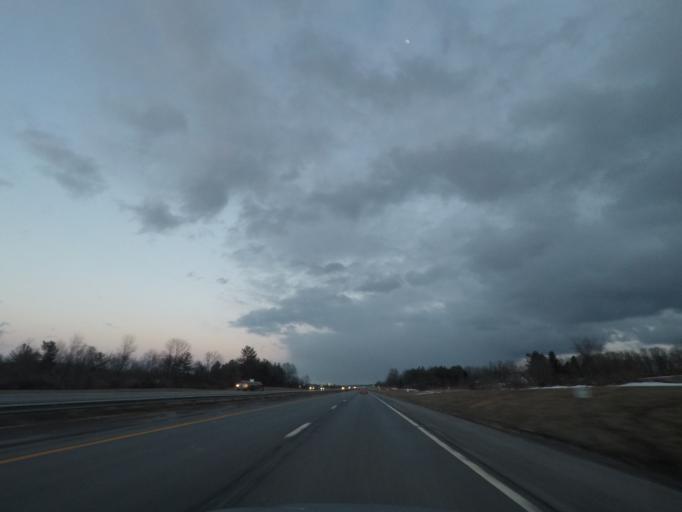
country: US
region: New York
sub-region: Montgomery County
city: Amsterdam
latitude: 42.9262
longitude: -74.2123
